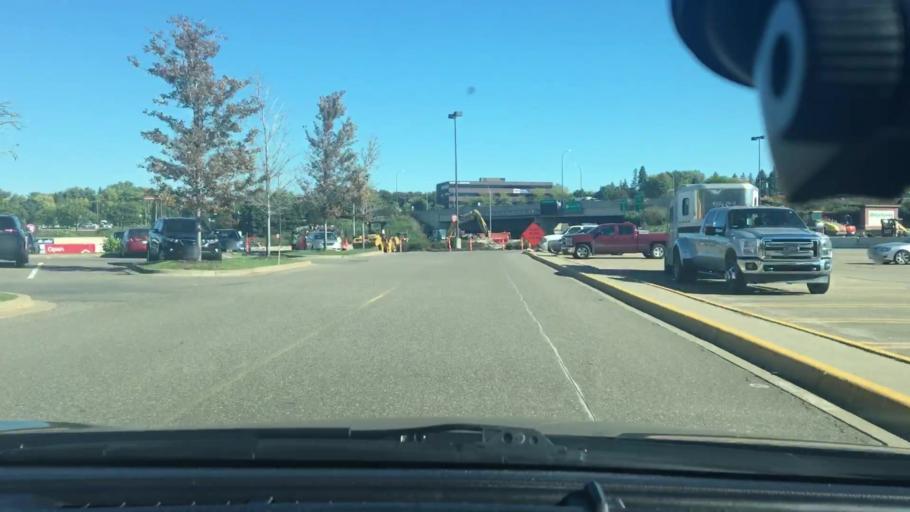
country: US
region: Minnesota
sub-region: Hennepin County
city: Minnetonka Mills
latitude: 44.9693
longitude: -93.4462
